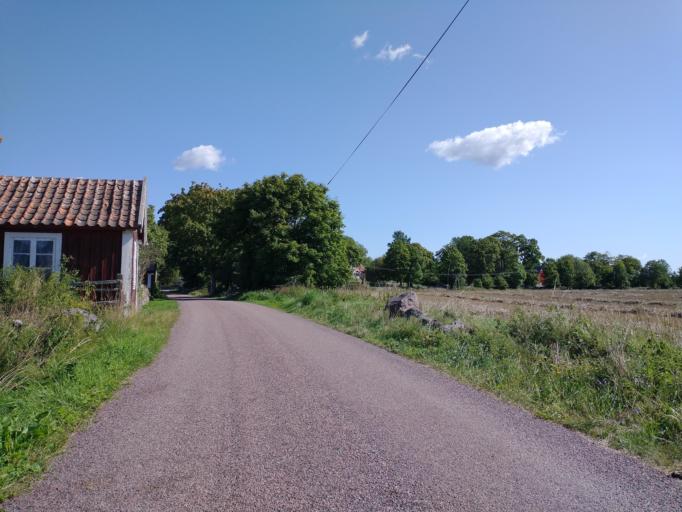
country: SE
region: Kalmar
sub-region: Kalmar Kommun
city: Lindsdal
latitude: 56.7957
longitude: 16.2663
